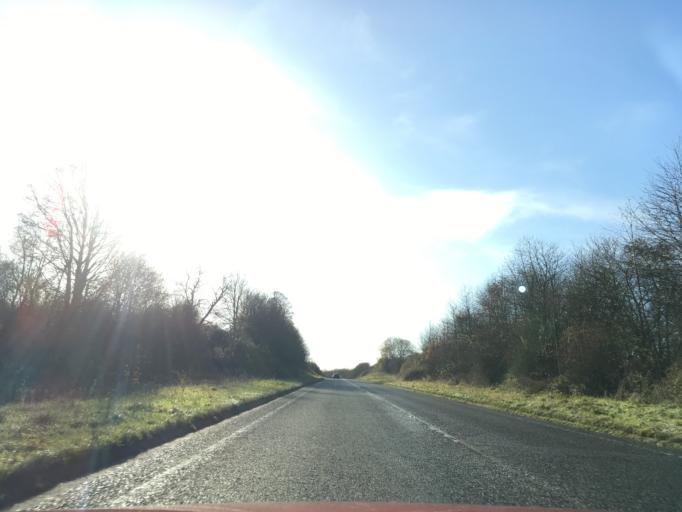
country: GB
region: England
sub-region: Wiltshire
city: Burbage
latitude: 51.3594
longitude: -1.6764
